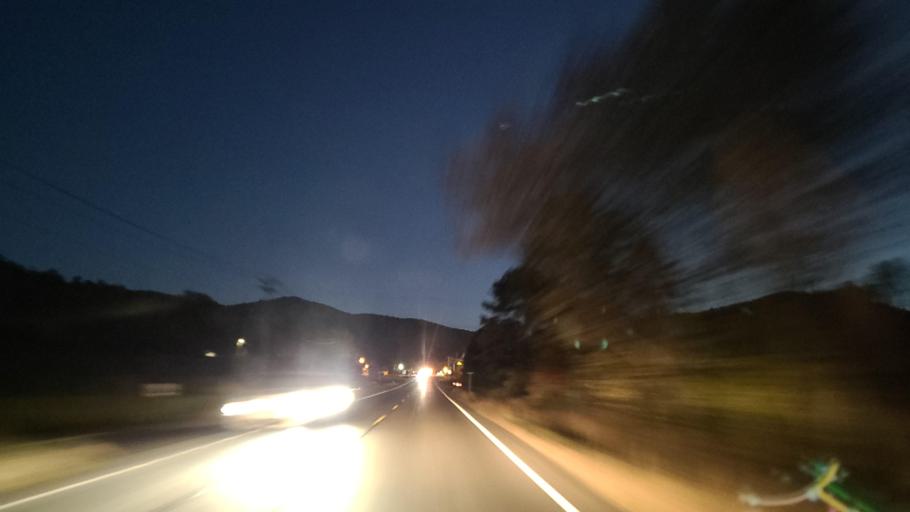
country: US
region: North Carolina
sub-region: Clay County
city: Hayesville
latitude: 34.9762
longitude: -83.8260
